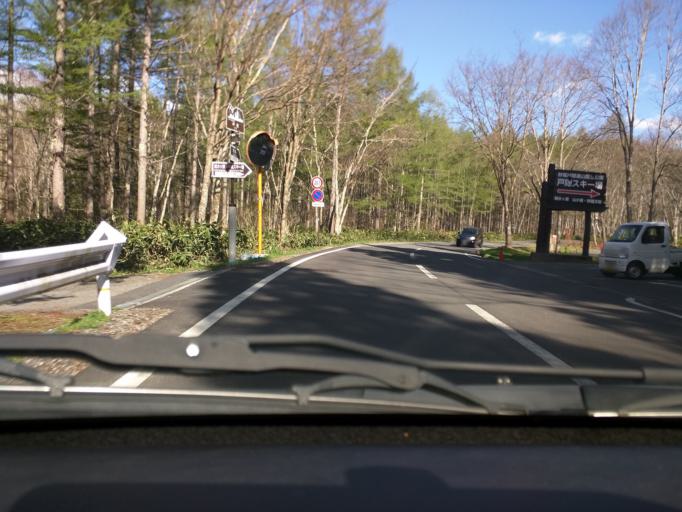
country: JP
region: Nagano
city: Nagano-shi
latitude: 36.7433
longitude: 138.0821
